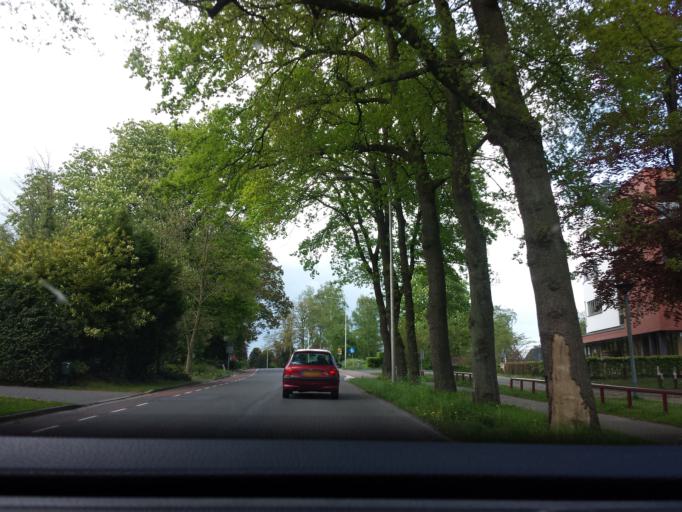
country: NL
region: Gelderland
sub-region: Gemeente Lochem
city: Lochem
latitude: 52.1495
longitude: 6.4199
